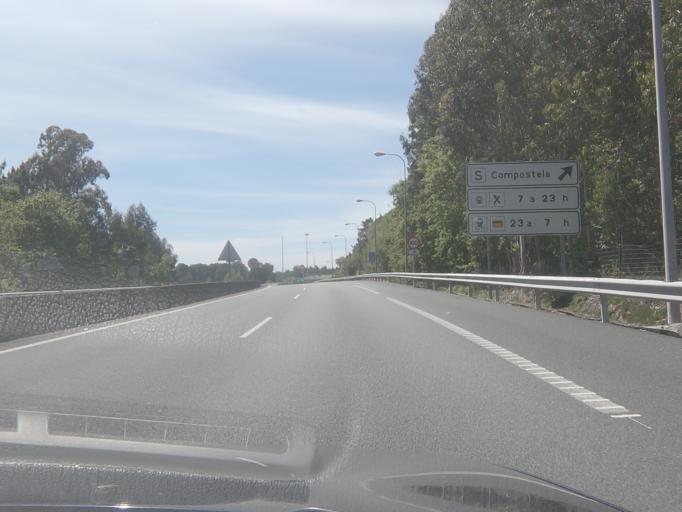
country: ES
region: Galicia
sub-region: Provincia da Coruna
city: Santiago de Compostela
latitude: 42.8122
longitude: -8.5814
